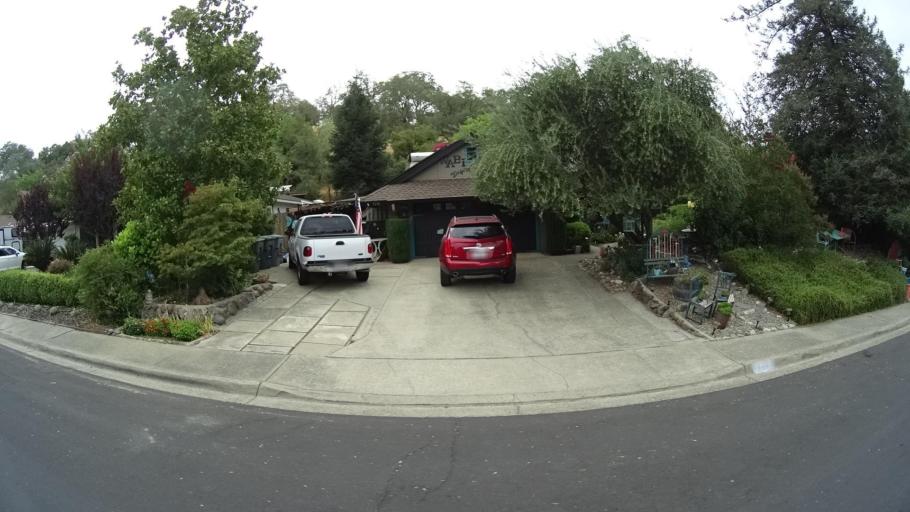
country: US
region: California
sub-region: Placer County
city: Rocklin
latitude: 38.7915
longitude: -121.2521
